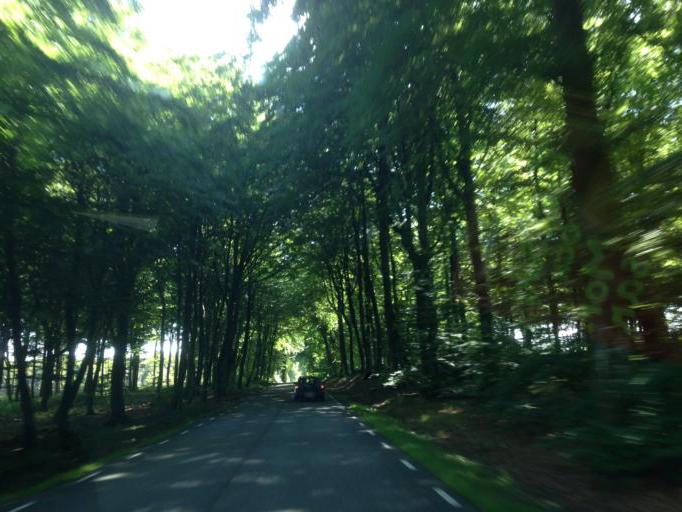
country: SE
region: Skane
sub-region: Simrishamns Kommun
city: Kivik
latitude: 55.6365
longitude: 14.1989
